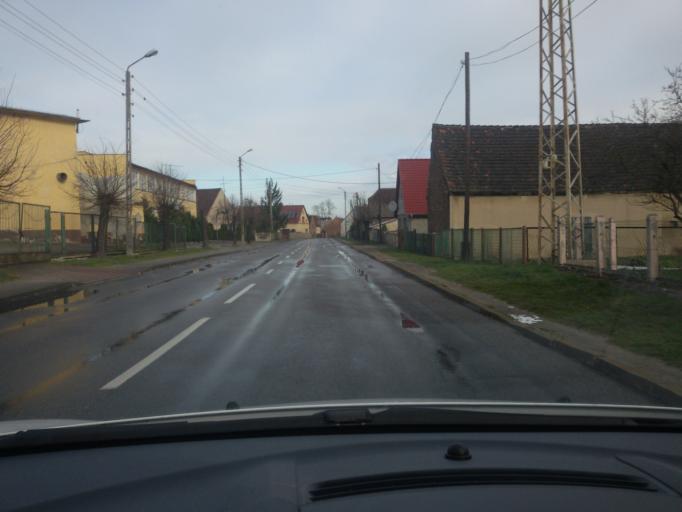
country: PL
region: Lower Silesian Voivodeship
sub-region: Powiat polkowicki
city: Gaworzyce
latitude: 51.6915
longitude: 15.9190
